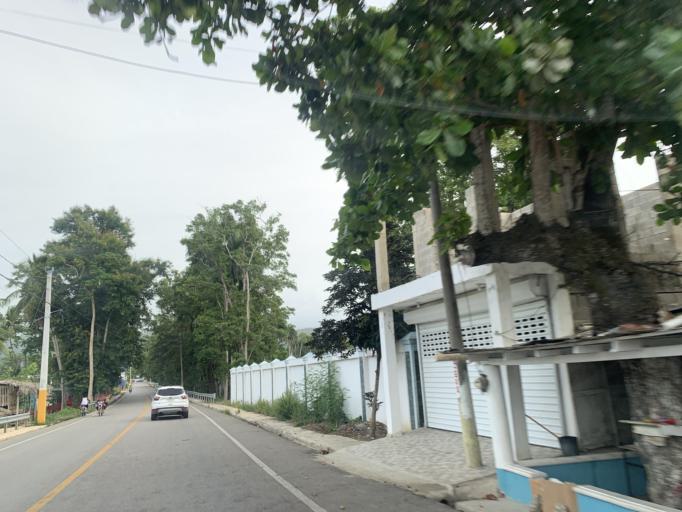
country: DO
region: Puerto Plata
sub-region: Puerto Plata
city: Puerto Plata
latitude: 19.7048
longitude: -70.6249
